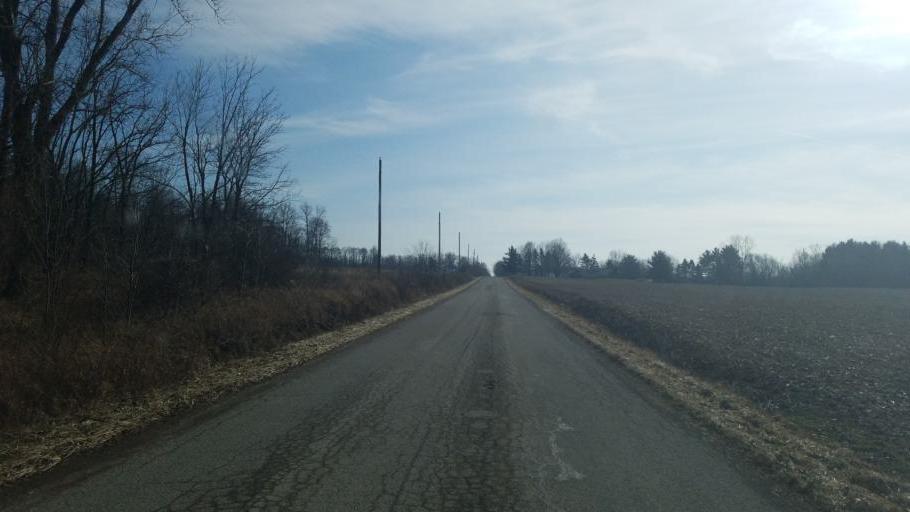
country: US
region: Ohio
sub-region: Crawford County
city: Crestline
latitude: 40.6988
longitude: -82.6893
